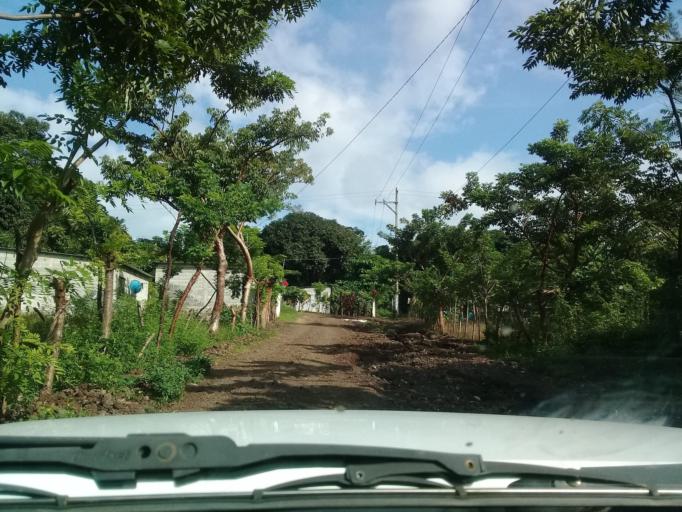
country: MX
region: Veracruz
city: Catemaco
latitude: 18.4342
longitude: -95.1297
